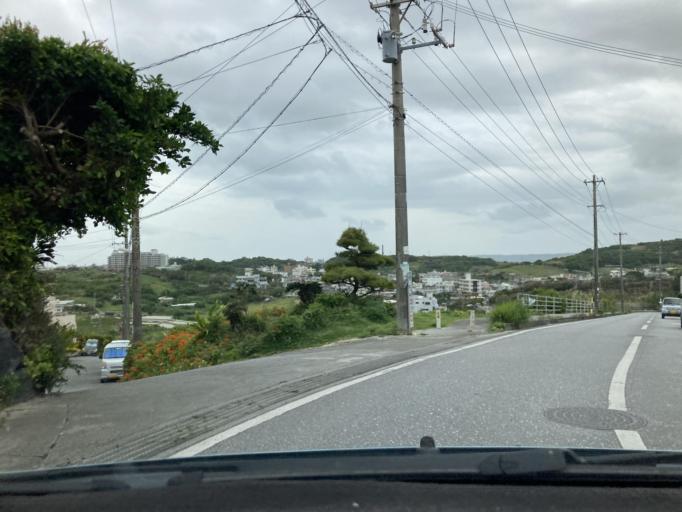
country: JP
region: Okinawa
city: Ginowan
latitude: 26.2364
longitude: 127.7384
